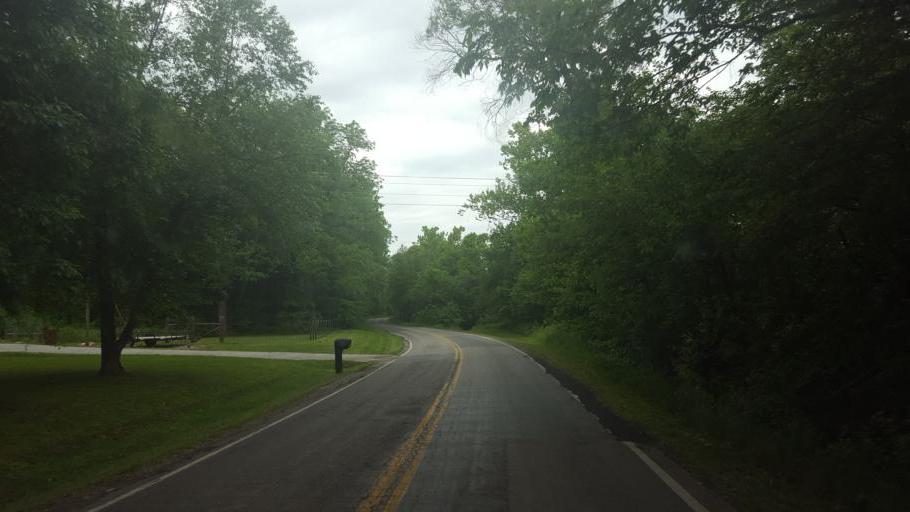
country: US
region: Missouri
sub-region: Moniteau County
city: California
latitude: 38.6494
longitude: -92.5717
